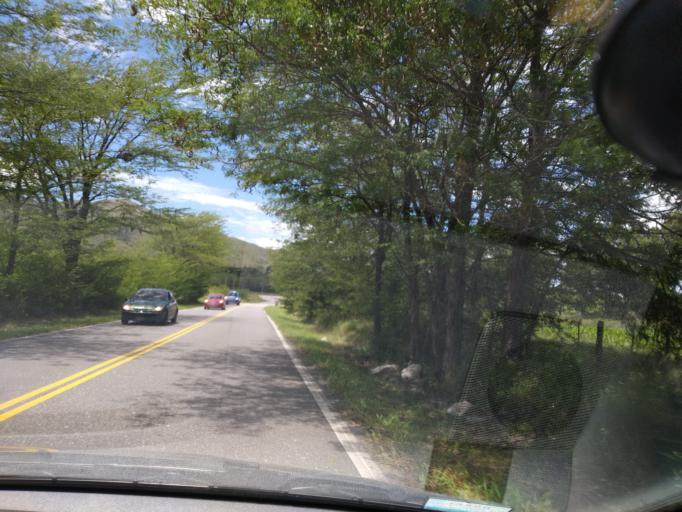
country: AR
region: Cordoba
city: Cuesta Blanca
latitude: -31.6047
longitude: -64.5622
